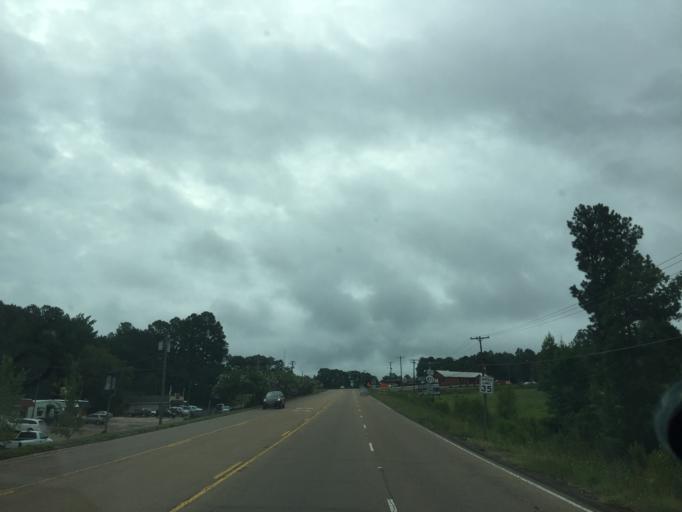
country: US
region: Mississippi
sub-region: Rankin County
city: Brandon
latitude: 32.2760
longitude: -89.9971
